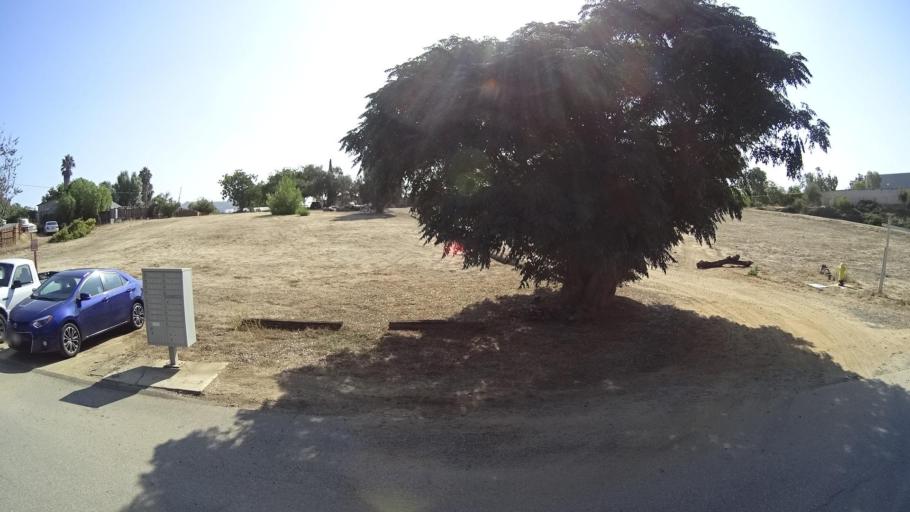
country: US
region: California
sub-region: San Diego County
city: Vista
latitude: 33.1740
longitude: -117.2148
